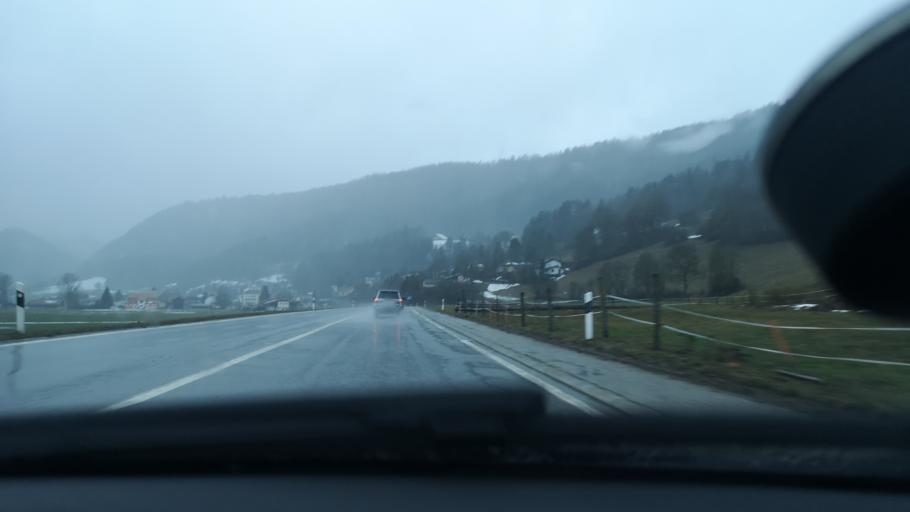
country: CH
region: Neuchatel
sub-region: Val-de-Travers District
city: Couvet
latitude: 46.9191
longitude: 6.6099
